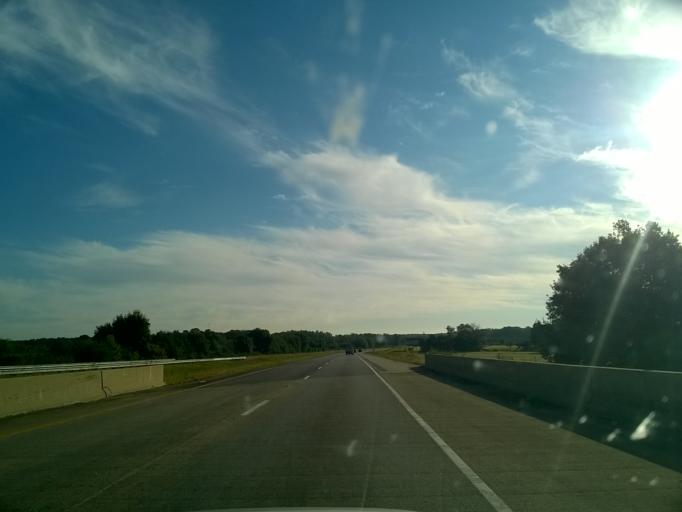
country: US
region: Indiana
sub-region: Gibson County
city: Oakland City
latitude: 38.1902
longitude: -87.3471
